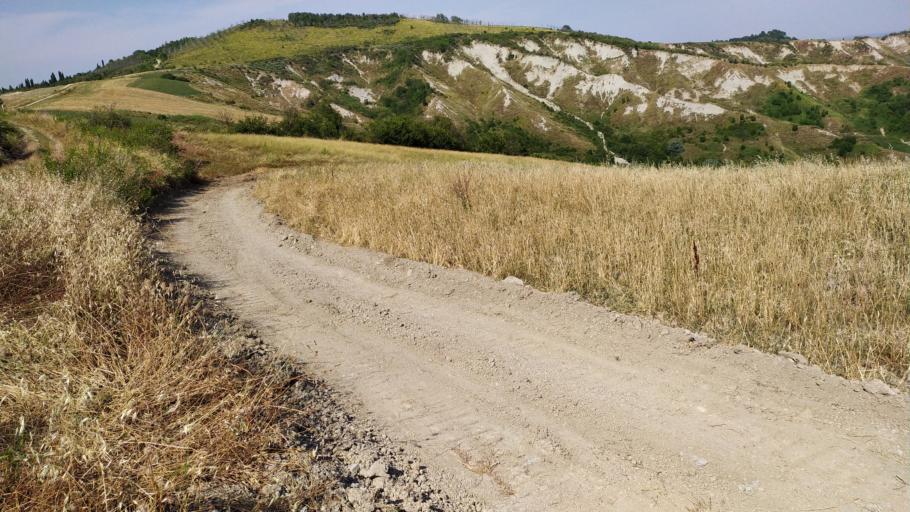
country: IT
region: Emilia-Romagna
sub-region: Forli-Cesena
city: Dovadola
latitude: 44.1613
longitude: 11.8951
